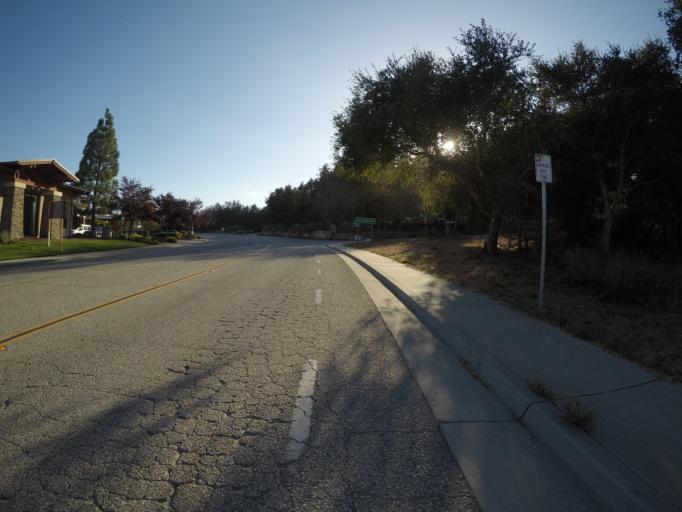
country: US
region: California
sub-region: Santa Cruz County
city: Scotts Valley
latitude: 37.0366
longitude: -122.0229
